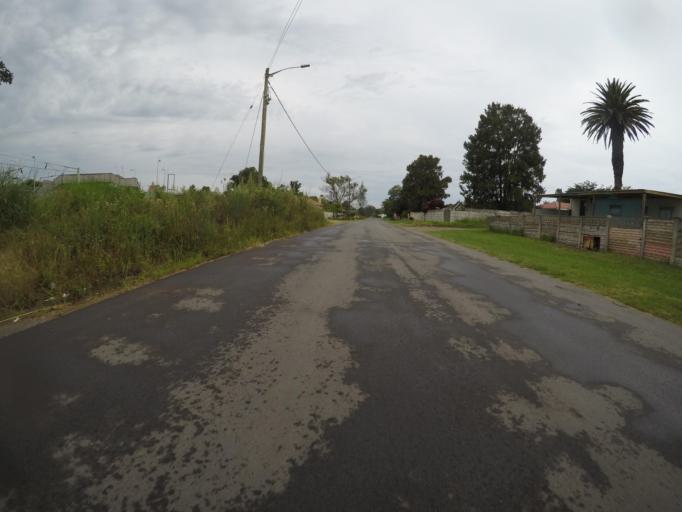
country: ZA
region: Eastern Cape
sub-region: Buffalo City Metropolitan Municipality
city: East London
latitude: -32.9660
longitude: 27.8310
